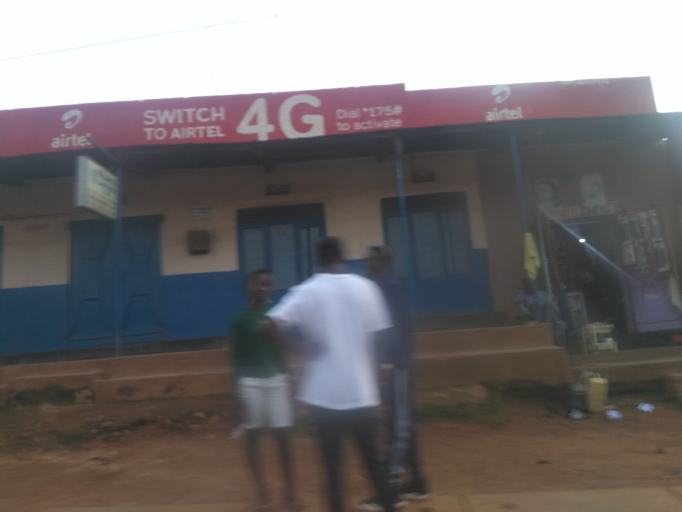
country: UG
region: Central Region
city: Kampala Central Division
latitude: 0.3476
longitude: 32.5735
